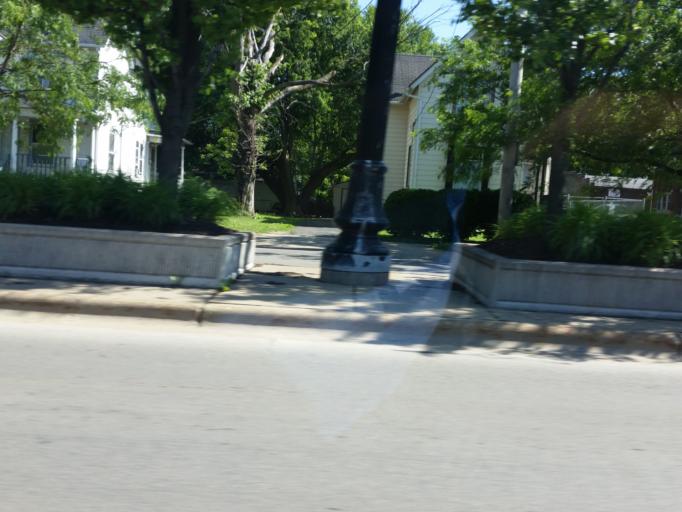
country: US
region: Illinois
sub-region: Winnebago County
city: Rockford
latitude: 42.2638
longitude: -89.0756
